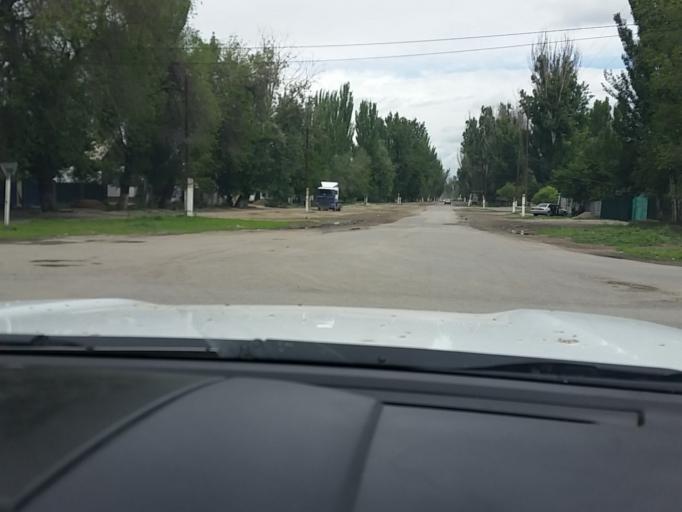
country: KZ
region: Almaty Oblysy
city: Zharkent
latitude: 44.1608
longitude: 79.9998
